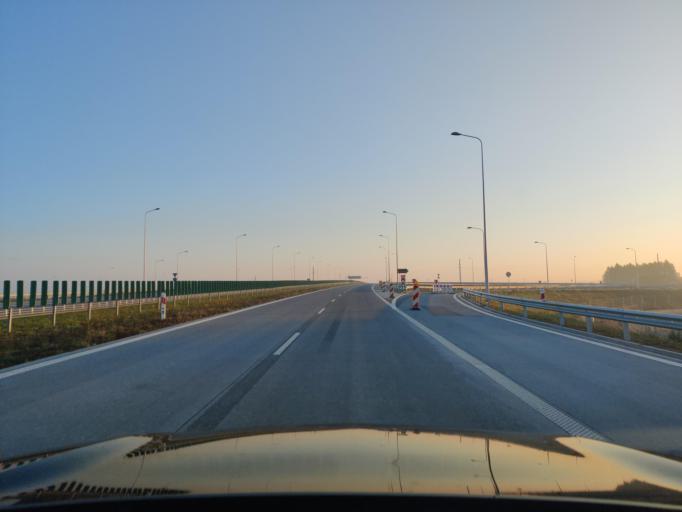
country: PL
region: Masovian Voivodeship
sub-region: Powiat mlawski
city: Wisniewo
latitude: 53.0715
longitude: 20.3743
